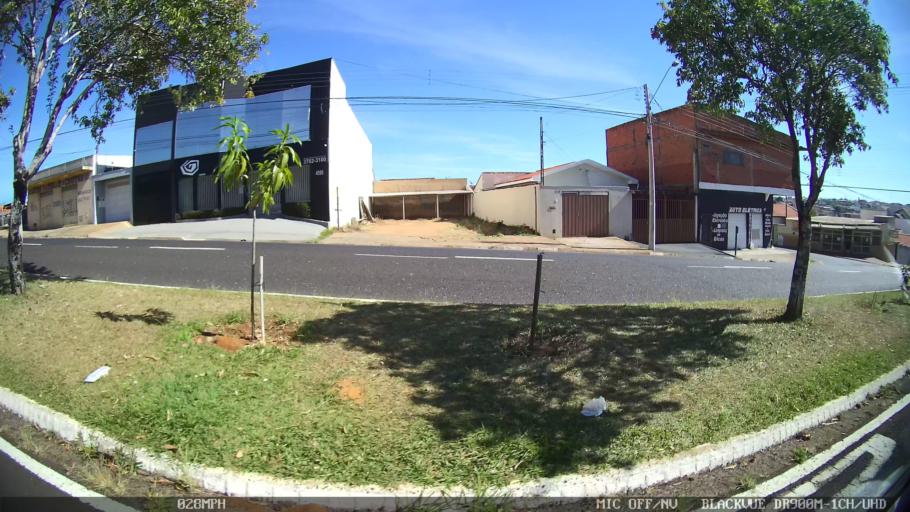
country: BR
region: Sao Paulo
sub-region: Franca
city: Franca
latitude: -20.5554
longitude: -47.3717
